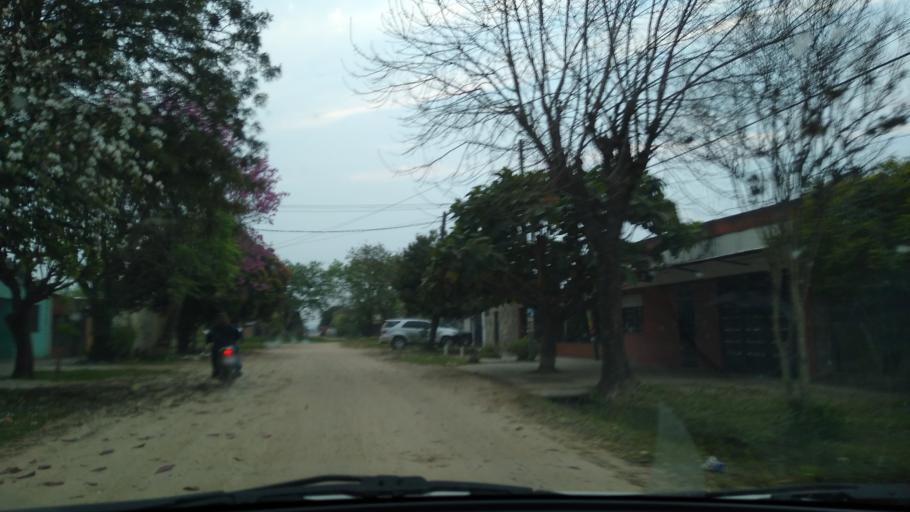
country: AR
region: Chaco
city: Barranqueras
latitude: -27.4880
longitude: -58.9523
